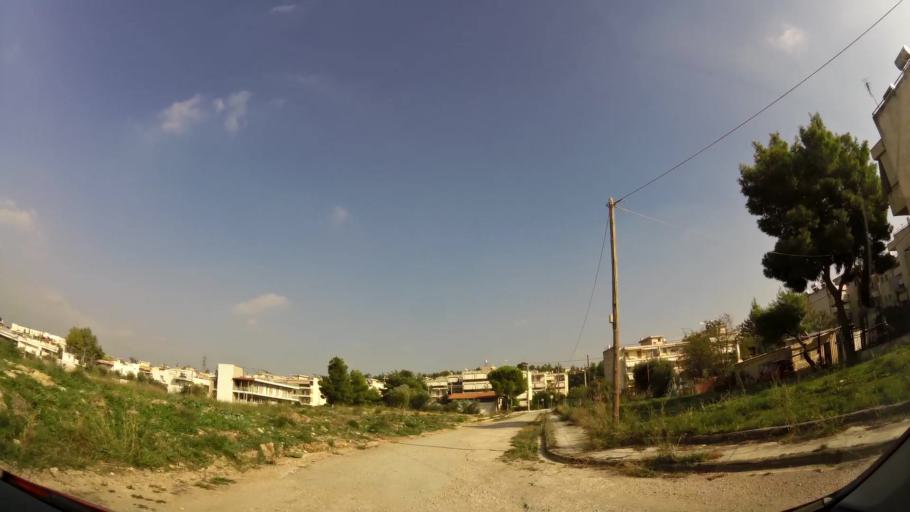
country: GR
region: Attica
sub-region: Nomarchia Dytikis Attikis
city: Zefyri
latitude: 38.0821
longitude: 23.7177
